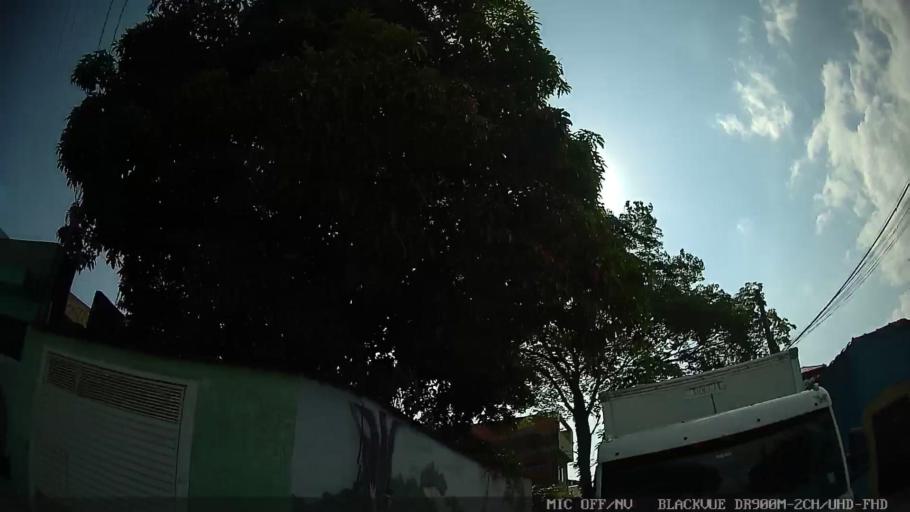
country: BR
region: Sao Paulo
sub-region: Ferraz De Vasconcelos
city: Ferraz de Vasconcelos
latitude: -23.5056
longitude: -46.4464
